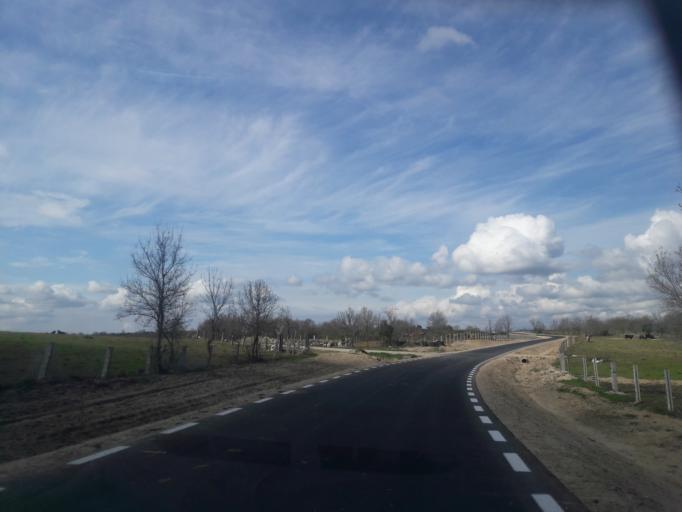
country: ES
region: Castille and Leon
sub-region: Provincia de Salamanca
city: Monleon
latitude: 40.5359
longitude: -5.8211
